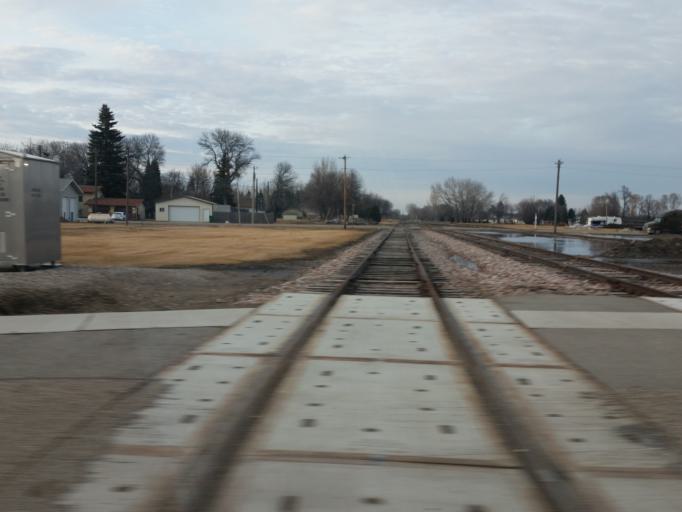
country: US
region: North Dakota
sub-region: Traill County
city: Mayville
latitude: 47.4985
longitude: -97.3701
